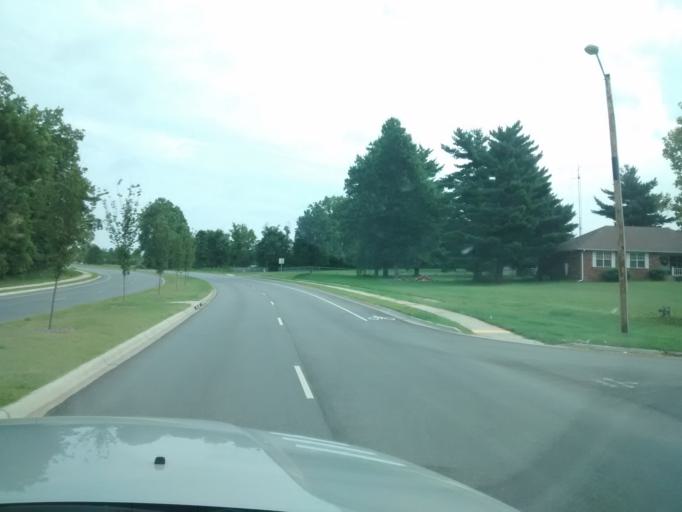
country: US
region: Arkansas
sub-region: Washington County
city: Springdale
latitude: 36.1436
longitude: -94.1175
